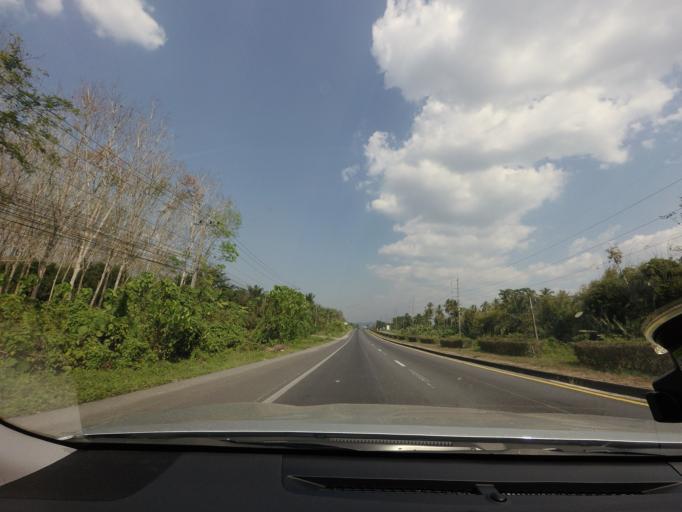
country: TH
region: Phangnga
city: Thap Put
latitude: 8.5085
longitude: 98.6610
